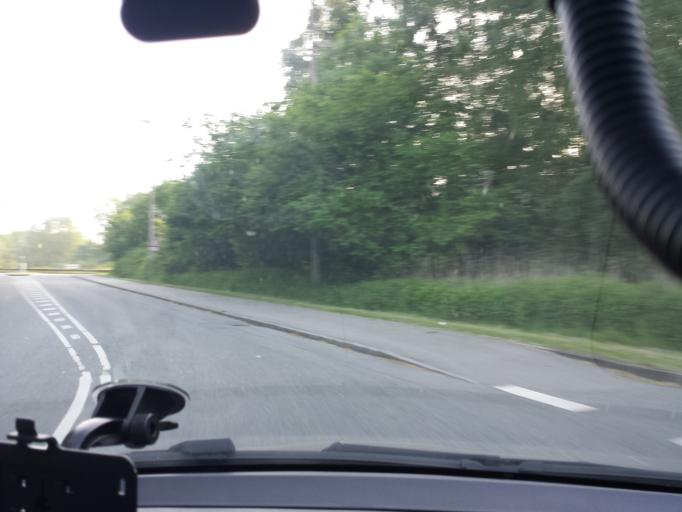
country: DK
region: Capital Region
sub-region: Herlev Kommune
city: Herlev
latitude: 55.7074
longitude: 12.4267
